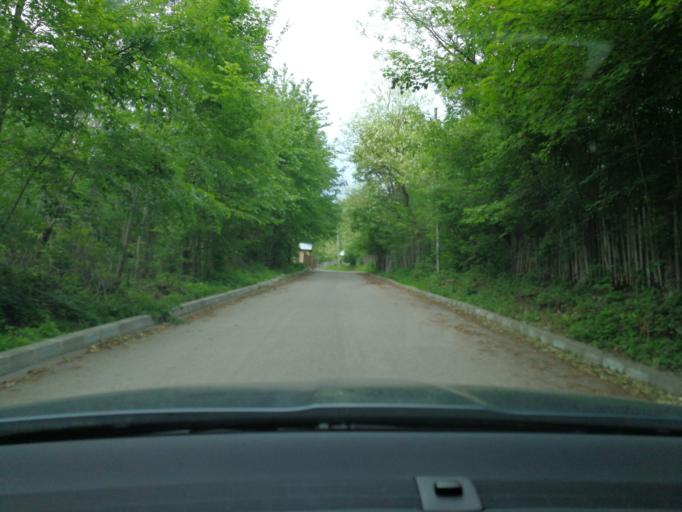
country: RO
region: Prahova
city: Cornu de Sus
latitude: 45.1667
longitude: 25.7056
